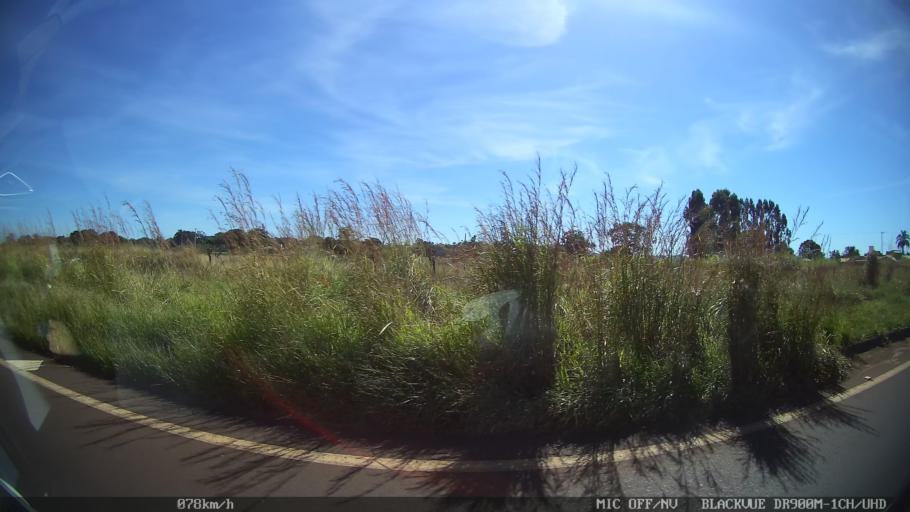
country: BR
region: Sao Paulo
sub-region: Franca
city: Franca
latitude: -20.5472
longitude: -47.4790
